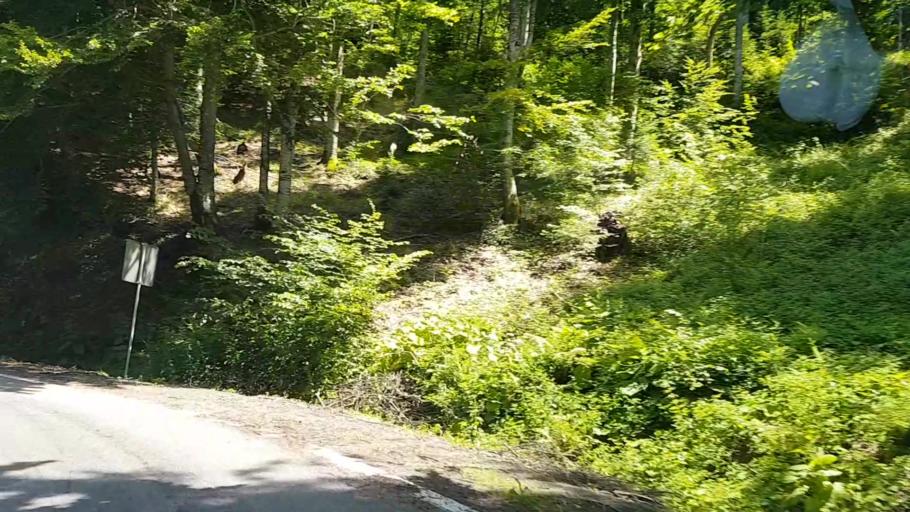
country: RO
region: Sibiu
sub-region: Comuna Cartisoara
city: Cartisoara
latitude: 45.6678
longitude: 24.5777
